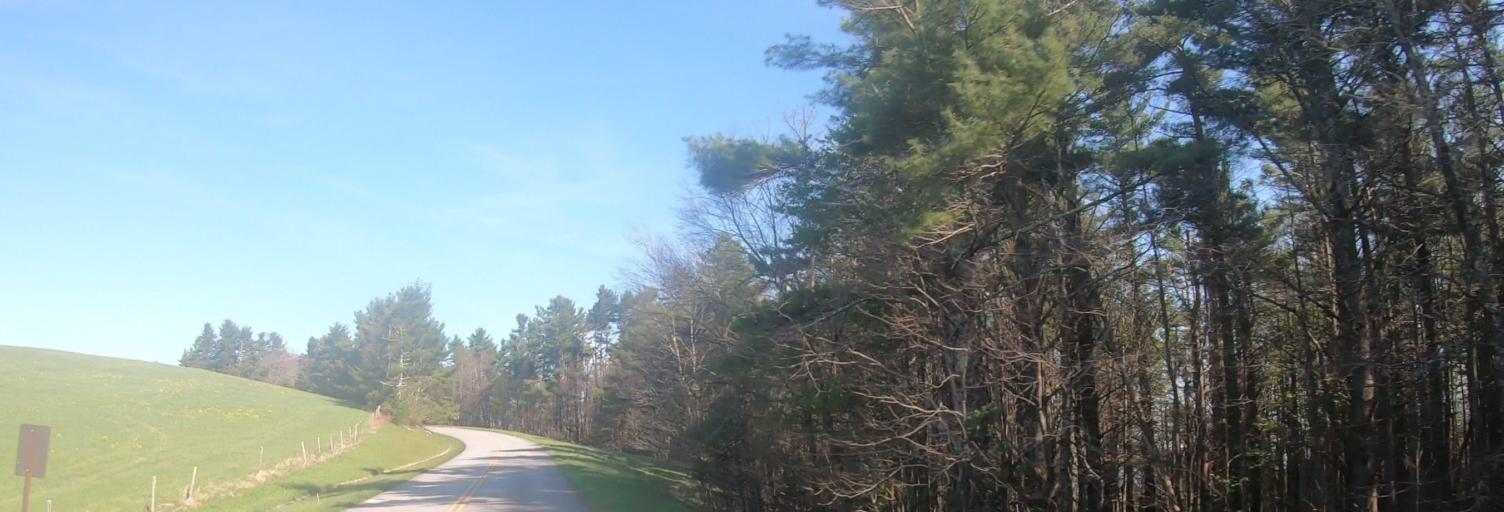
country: US
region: North Carolina
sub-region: Watauga County
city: Boone
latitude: 36.2252
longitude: -81.5187
